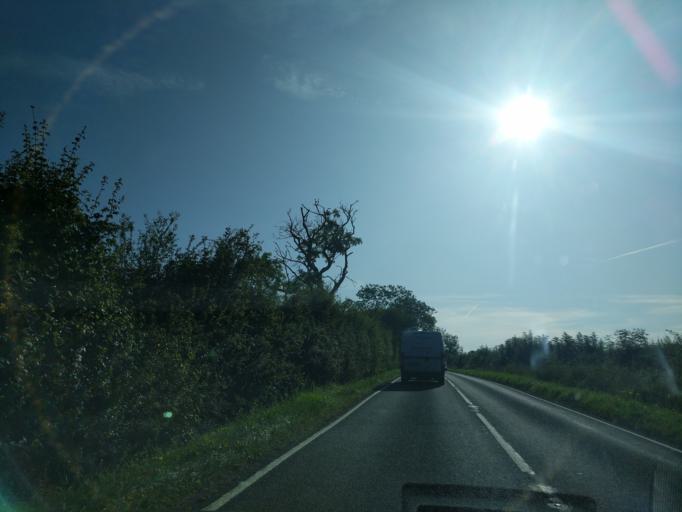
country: GB
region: England
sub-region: District of Rutland
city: Clipsham
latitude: 52.8076
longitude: -0.4998
